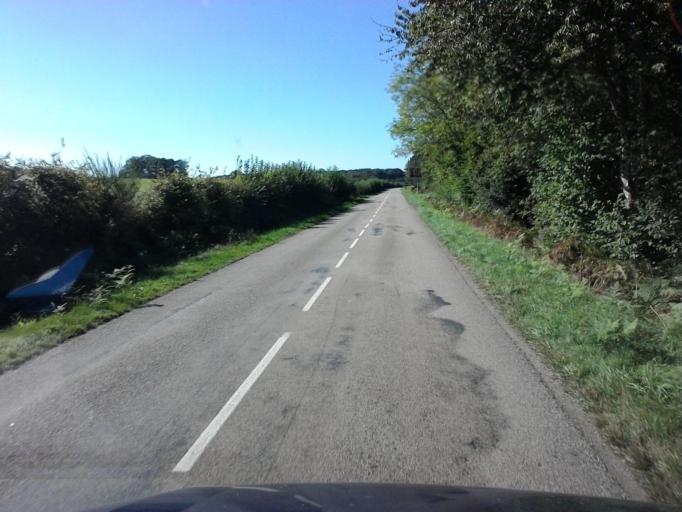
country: FR
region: Bourgogne
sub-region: Departement de la Nievre
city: Lormes
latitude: 47.2784
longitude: 3.8305
